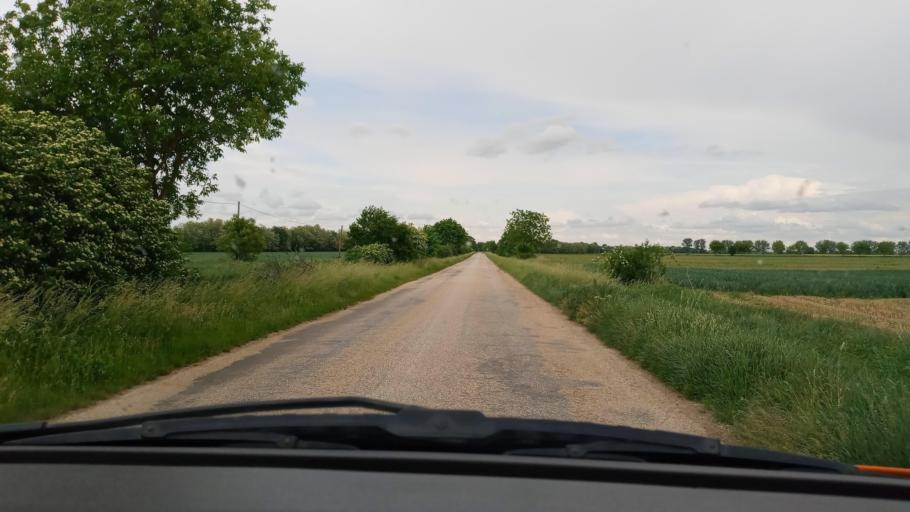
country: HU
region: Baranya
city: Harkany
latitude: 45.9145
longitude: 18.1487
